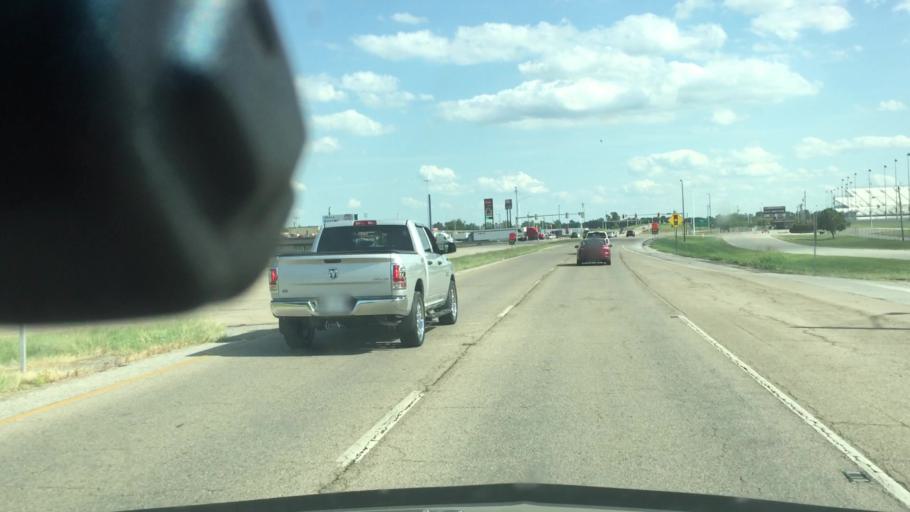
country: US
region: Illinois
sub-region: Saint Clair County
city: East Saint Louis
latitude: 38.6549
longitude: -90.1341
